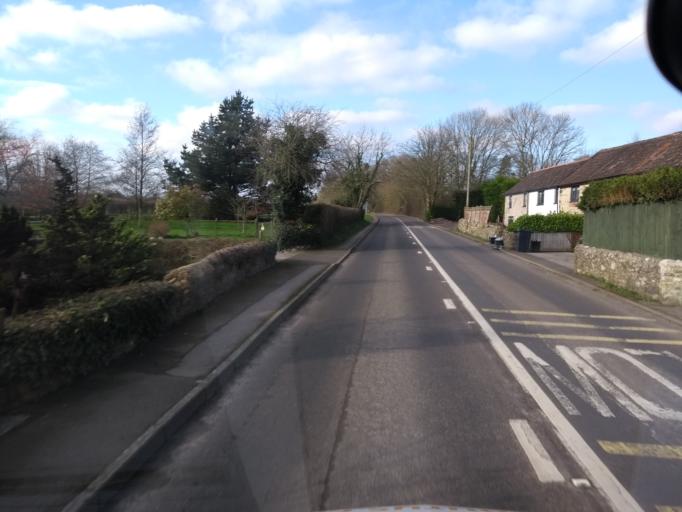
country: GB
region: England
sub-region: Somerset
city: Ilminster
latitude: 50.9298
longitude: -2.9583
